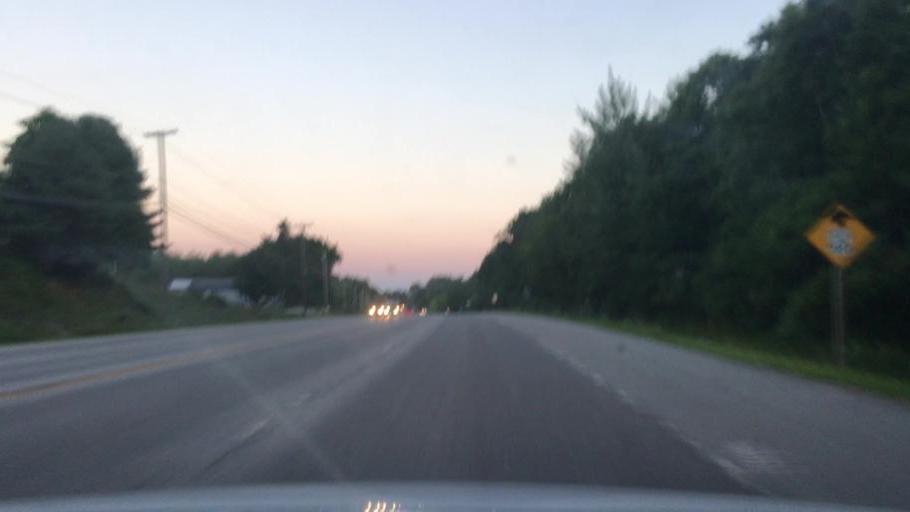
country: US
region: Maine
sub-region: Androscoggin County
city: Auburn
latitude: 44.1496
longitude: -70.2307
